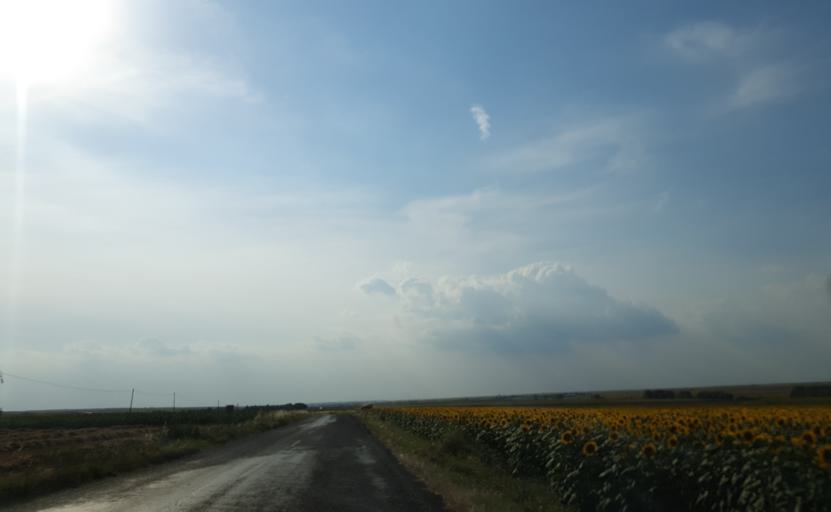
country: TR
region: Tekirdag
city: Muratli
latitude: 41.2123
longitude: 27.4454
